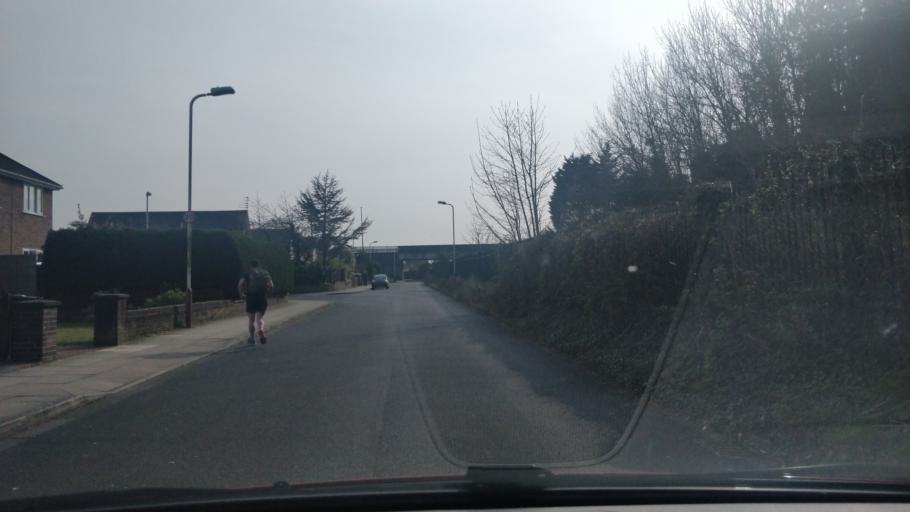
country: GB
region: England
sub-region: Sefton
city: Formby
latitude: 53.6001
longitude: -3.0440
